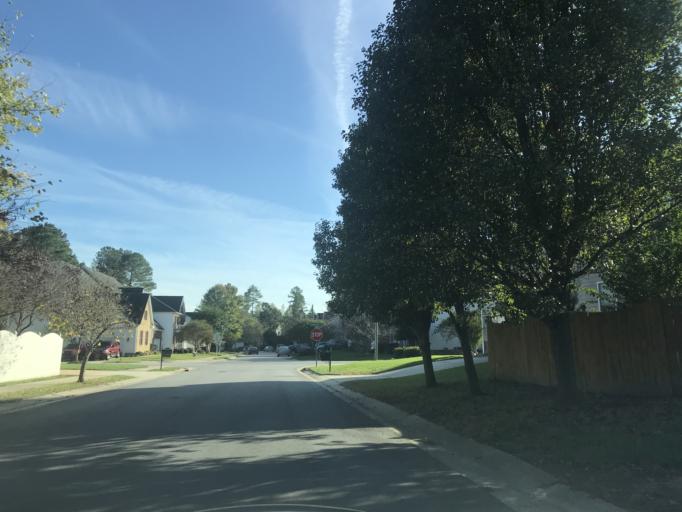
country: US
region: North Carolina
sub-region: Wake County
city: Rolesville
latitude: 35.8926
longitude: -78.5437
